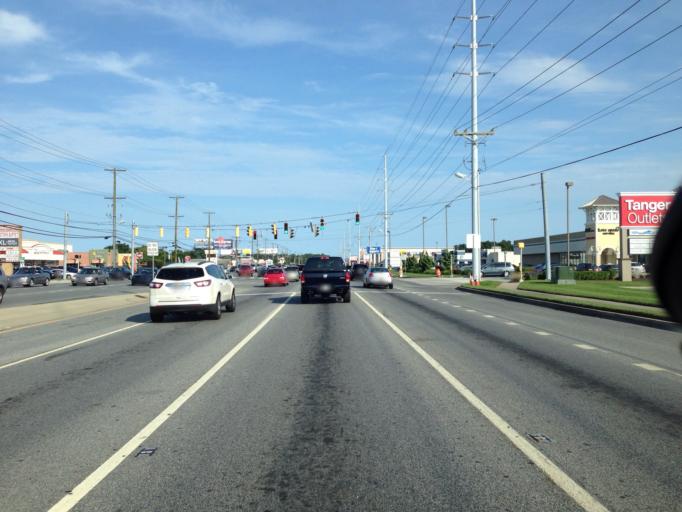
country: US
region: Delaware
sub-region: Sussex County
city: Lewes
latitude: 38.7354
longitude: -75.1395
